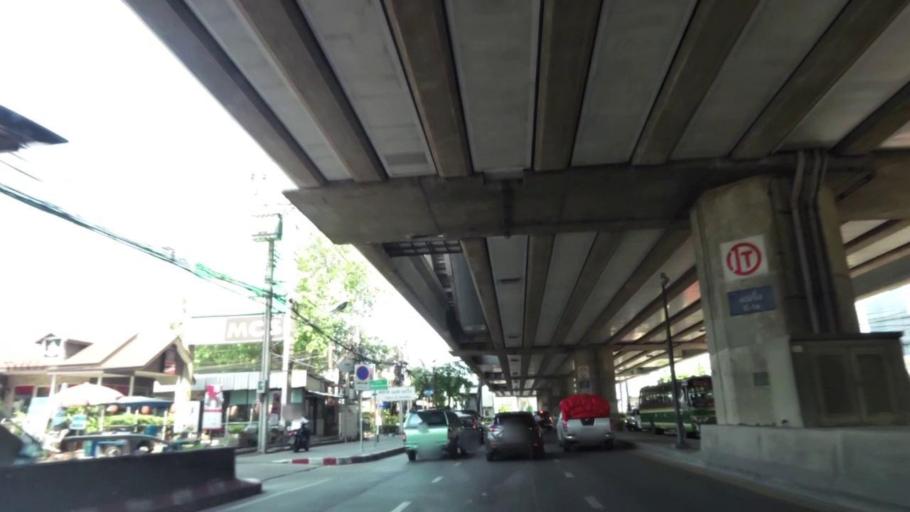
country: TH
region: Bangkok
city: Bang Na
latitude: 13.6608
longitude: 100.6016
